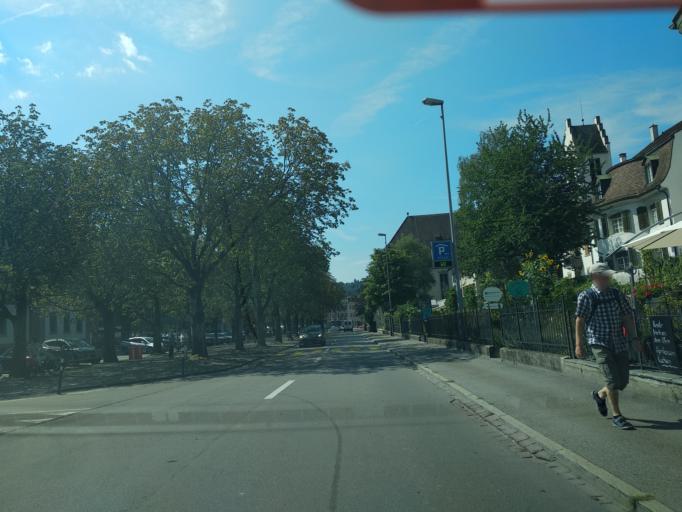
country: CH
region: Thurgau
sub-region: Frauenfeld District
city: Frauenfeld
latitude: 47.5567
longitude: 8.8992
